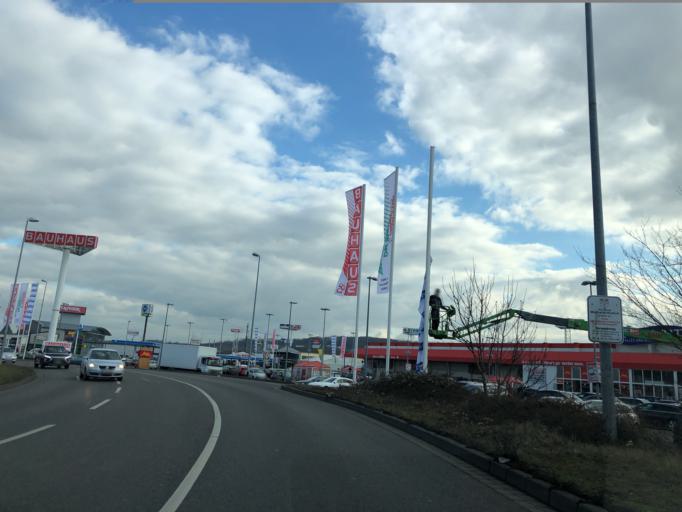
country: DE
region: Rheinland-Pfalz
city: Mulheim-Karlich
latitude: 50.3975
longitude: 7.5111
